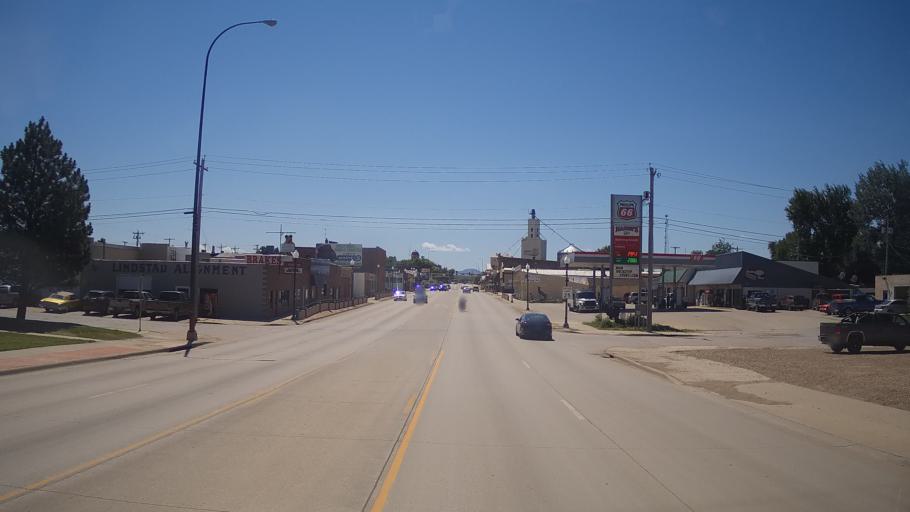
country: US
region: South Dakota
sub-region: Butte County
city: Belle Fourche
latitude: 44.6740
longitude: -103.8536
